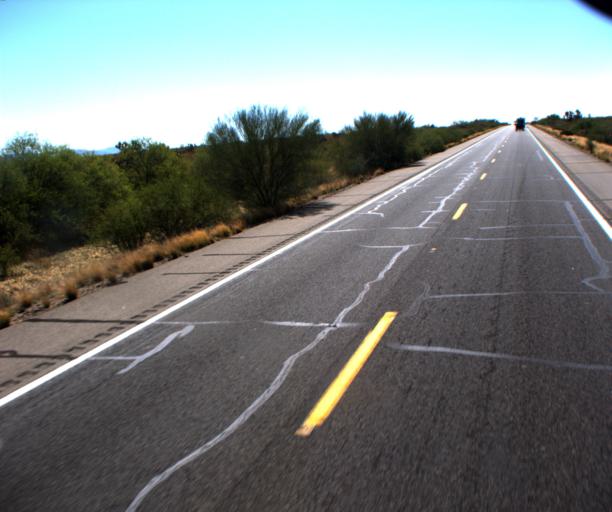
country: US
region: Arizona
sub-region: Yavapai County
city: Congress
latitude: 34.1686
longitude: -113.0156
